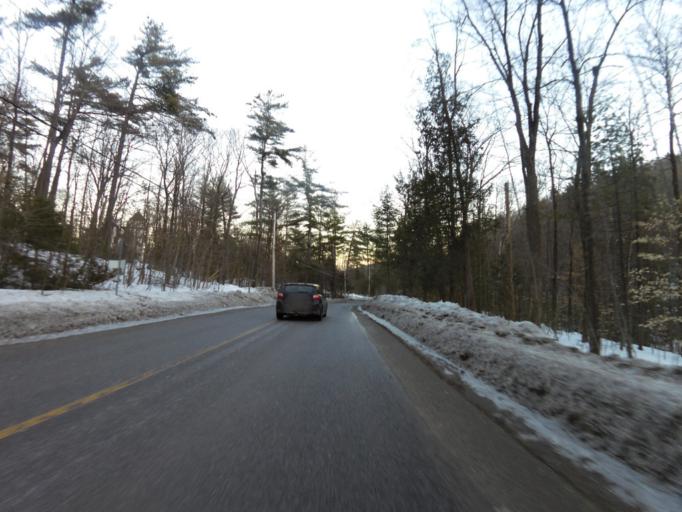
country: CA
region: Quebec
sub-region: Outaouais
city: Gatineau
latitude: 45.4847
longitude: -75.8082
